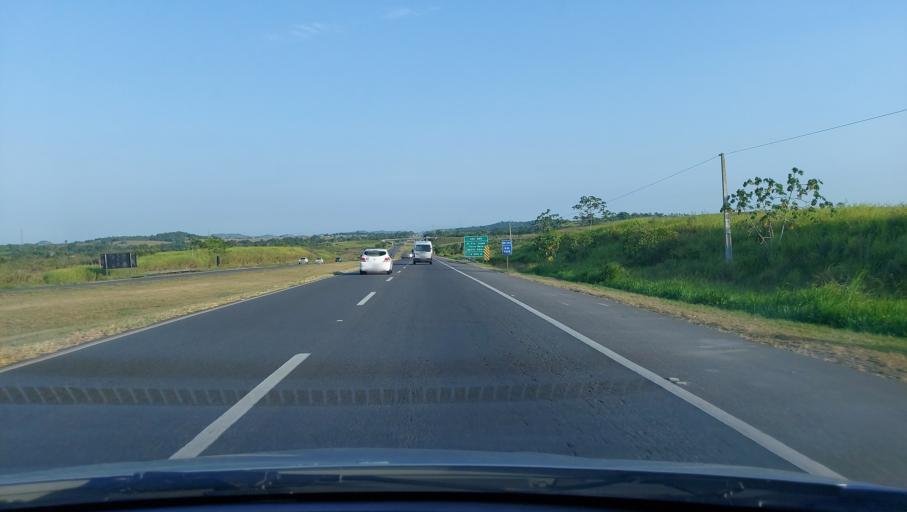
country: BR
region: Bahia
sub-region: Santo Amaro
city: Santo Amaro
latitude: -12.5263
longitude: -38.6080
